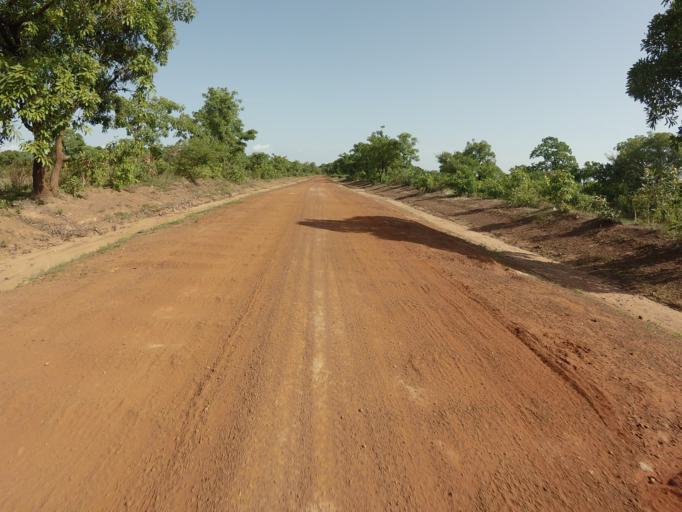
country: GH
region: Upper East
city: Bawku
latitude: 10.7438
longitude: -0.2004
